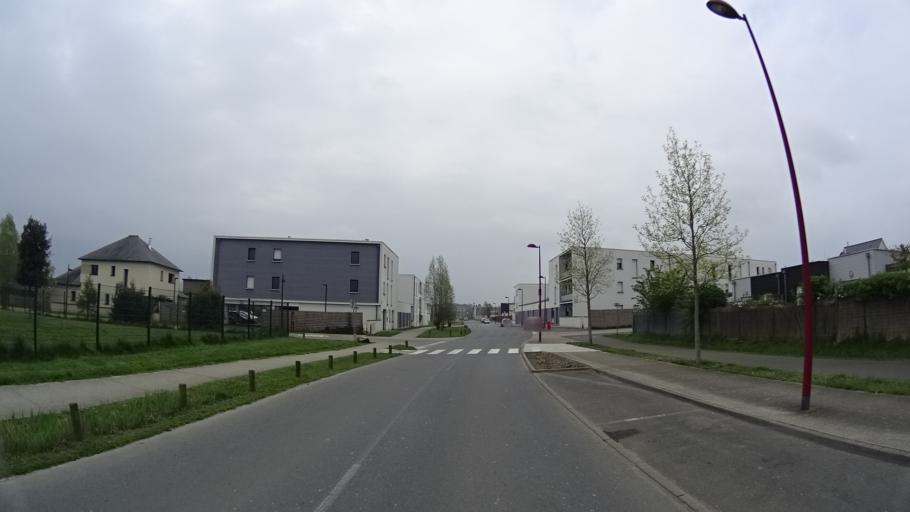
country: FR
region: Brittany
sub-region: Departement d'Ille-et-Vilaine
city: Saint-Gilles
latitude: 48.1548
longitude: -1.8393
